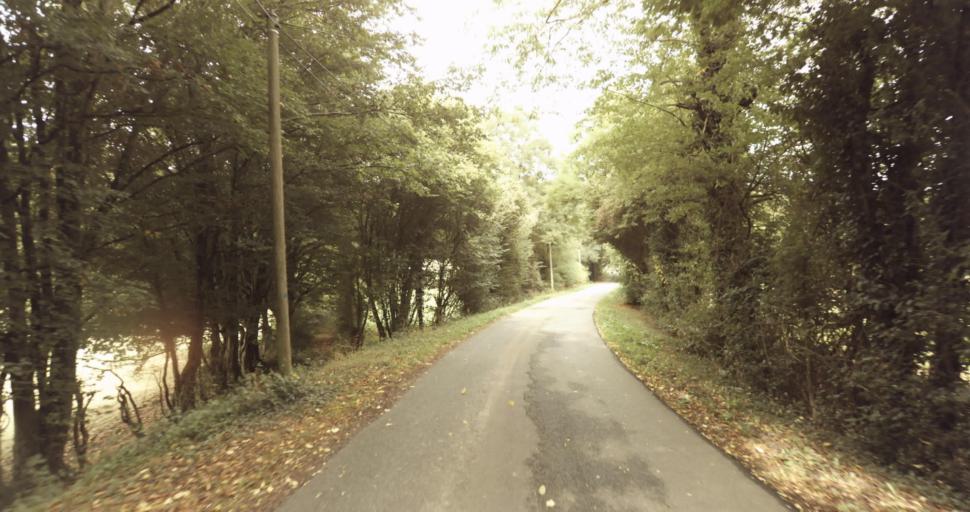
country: FR
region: Lower Normandy
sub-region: Departement du Calvados
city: Orbec
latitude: 48.9473
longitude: 0.3727
